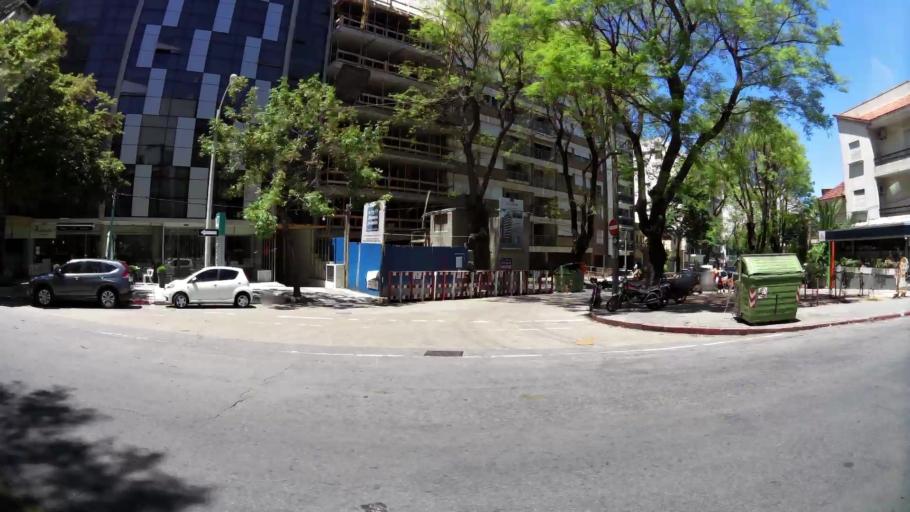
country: UY
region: Montevideo
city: Montevideo
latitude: -34.9204
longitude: -56.1566
